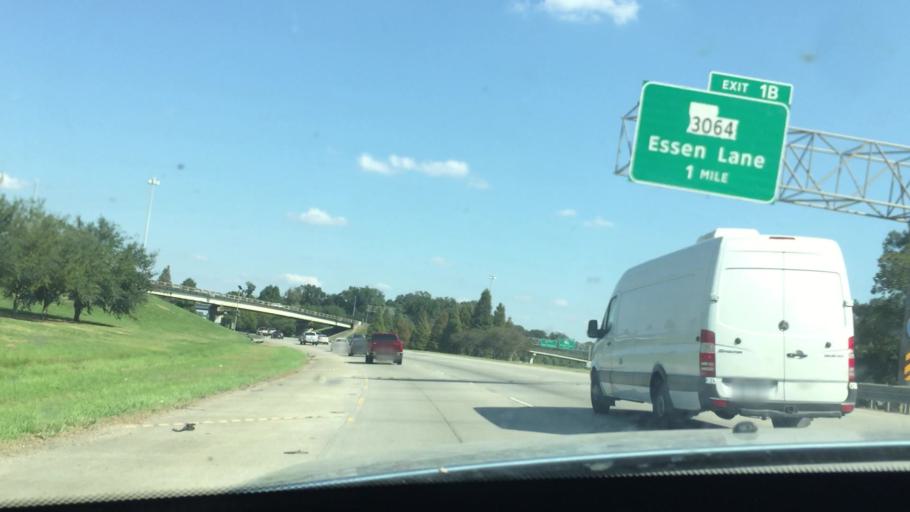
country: US
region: Louisiana
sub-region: East Baton Rouge Parish
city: Westminster
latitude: 30.4183
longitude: -91.1183
